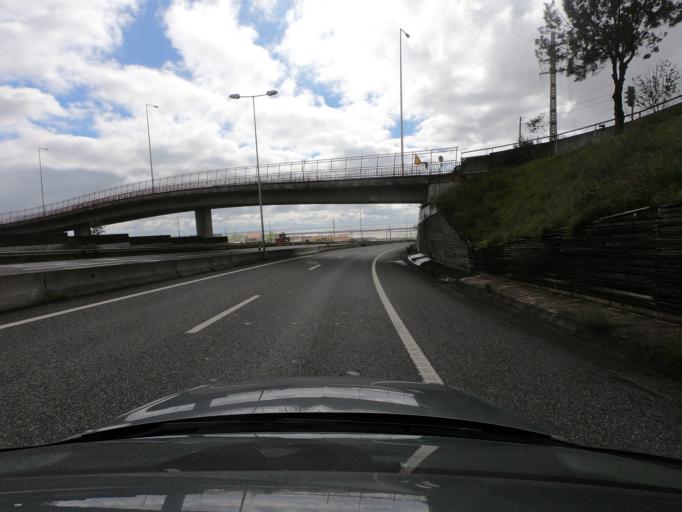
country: PT
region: Lisbon
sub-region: Loures
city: Santa Iria da Azoia
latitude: 38.8478
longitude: -9.0834
